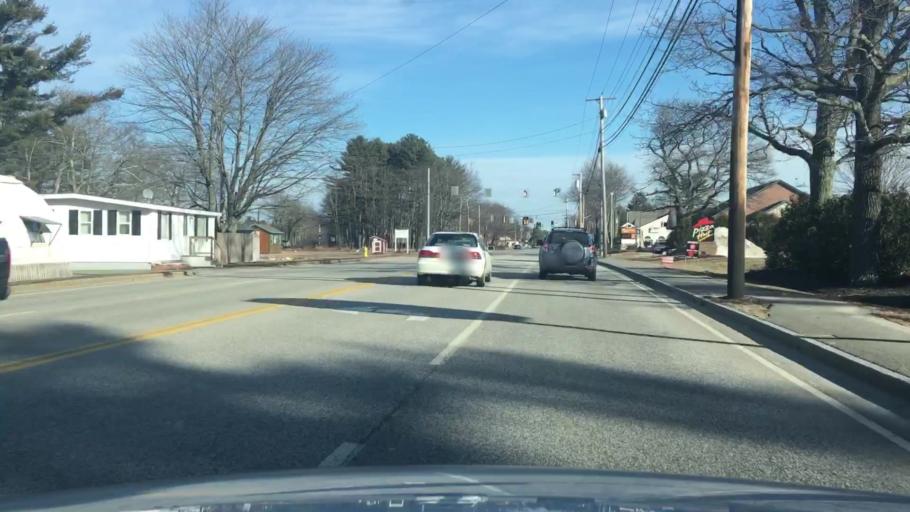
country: US
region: Maine
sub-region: Cumberland County
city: Brunswick
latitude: 43.9092
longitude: -69.9093
